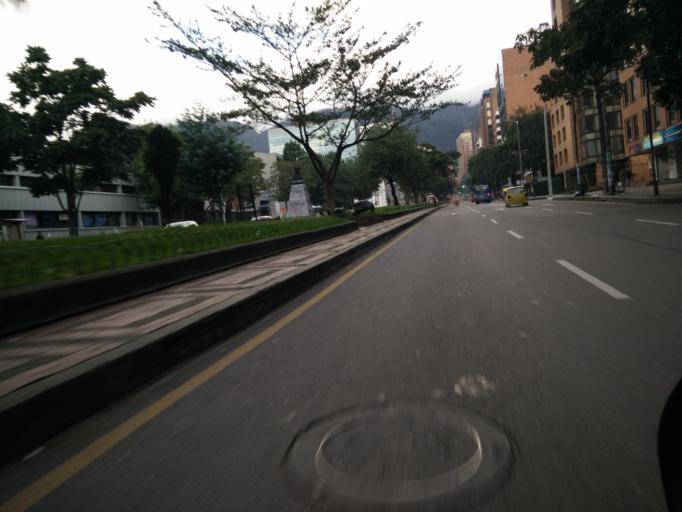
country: CO
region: Bogota D.C.
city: Barrio San Luis
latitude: 4.6582
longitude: -74.0604
